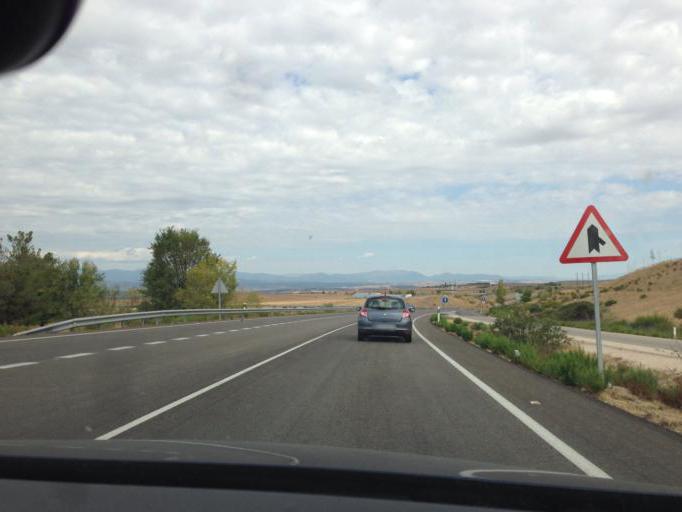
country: ES
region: Madrid
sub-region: Provincia de Madrid
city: Cobena
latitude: 40.5601
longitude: -3.5160
